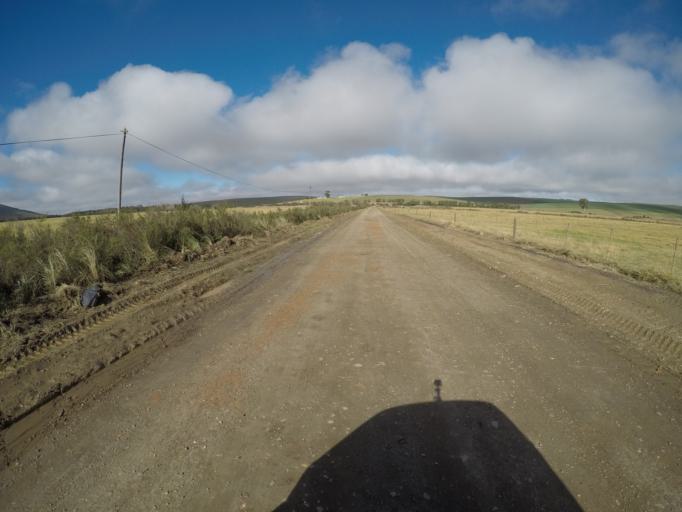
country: ZA
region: Western Cape
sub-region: Cape Winelands District Municipality
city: Ashton
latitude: -34.1223
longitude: 19.8388
